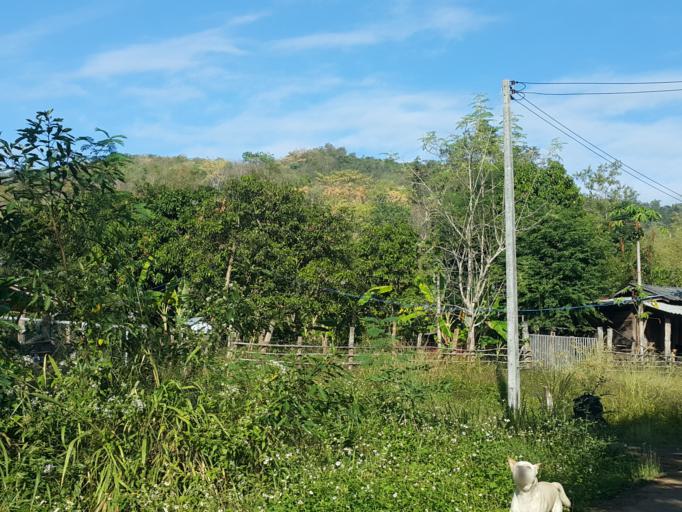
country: TH
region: Lampang
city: Mae Mo
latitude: 18.2813
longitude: 99.6398
